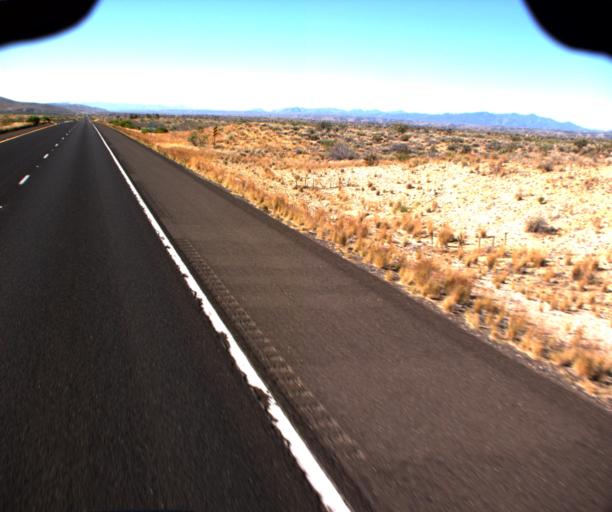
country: US
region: Arizona
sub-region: Mohave County
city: Kingman
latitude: 35.0708
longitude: -113.6659
